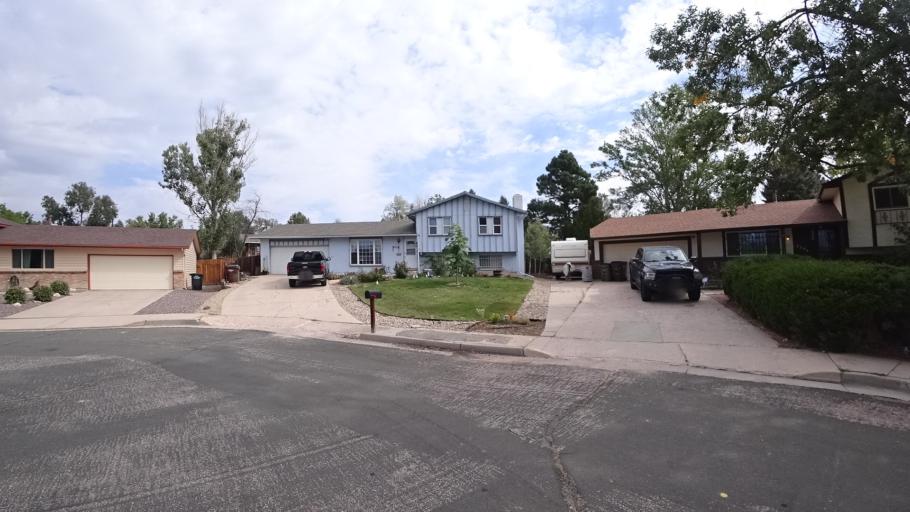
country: US
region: Colorado
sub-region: El Paso County
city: Cimarron Hills
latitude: 38.8481
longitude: -104.7279
